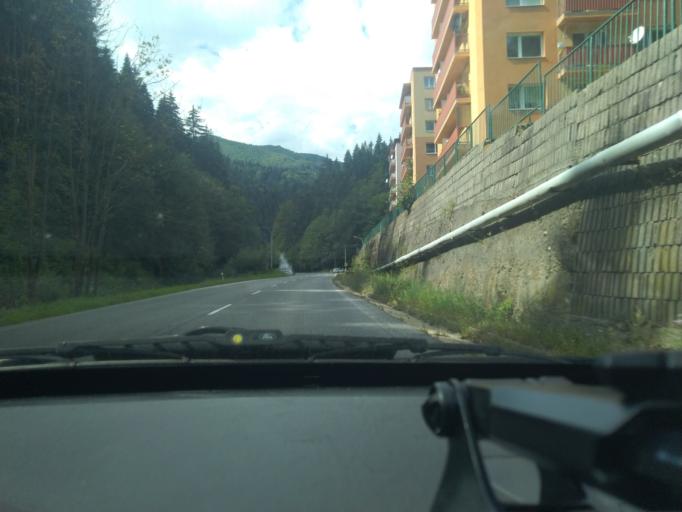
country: SK
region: Banskobystricky
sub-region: Okres Banska Bystrica
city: Banska Bystrica
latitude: 48.7959
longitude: 19.0683
